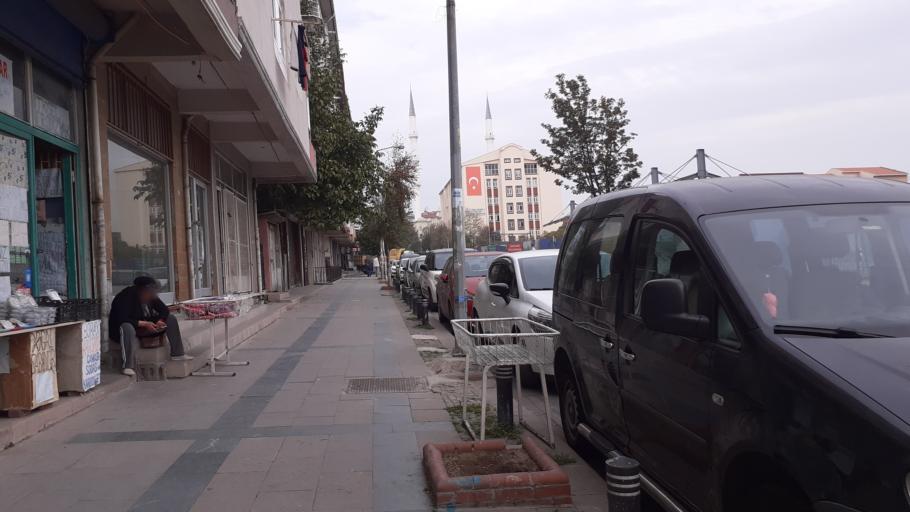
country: TR
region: Istanbul
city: Mahmutbey
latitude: 40.9896
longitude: 28.7829
